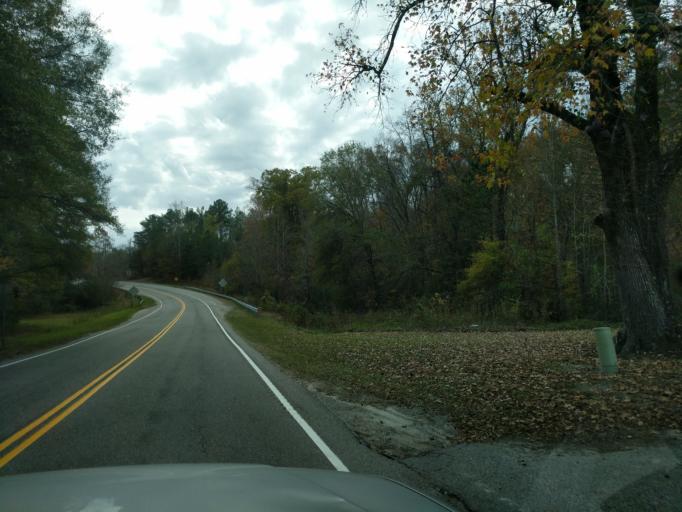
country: US
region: South Carolina
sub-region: Greenwood County
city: Ninety Six
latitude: 34.1796
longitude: -81.8667
